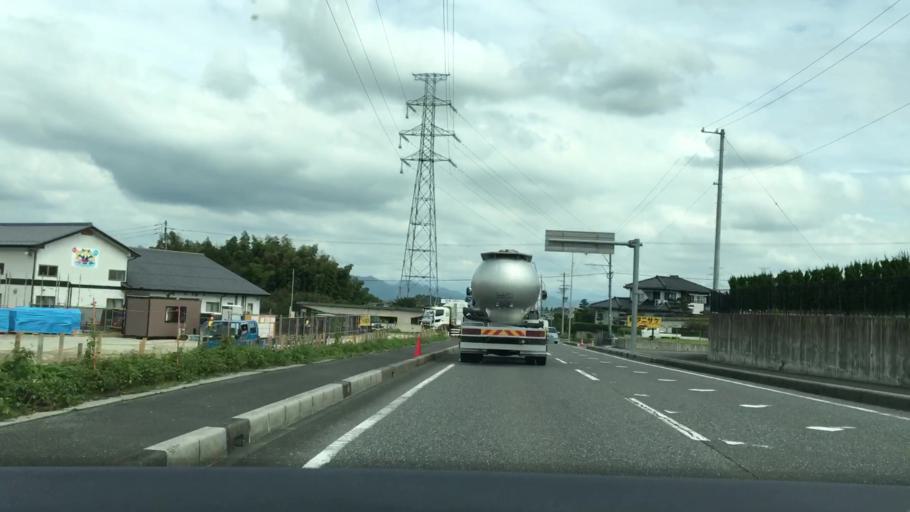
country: JP
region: Gifu
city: Godo
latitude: 35.4215
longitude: 136.5685
